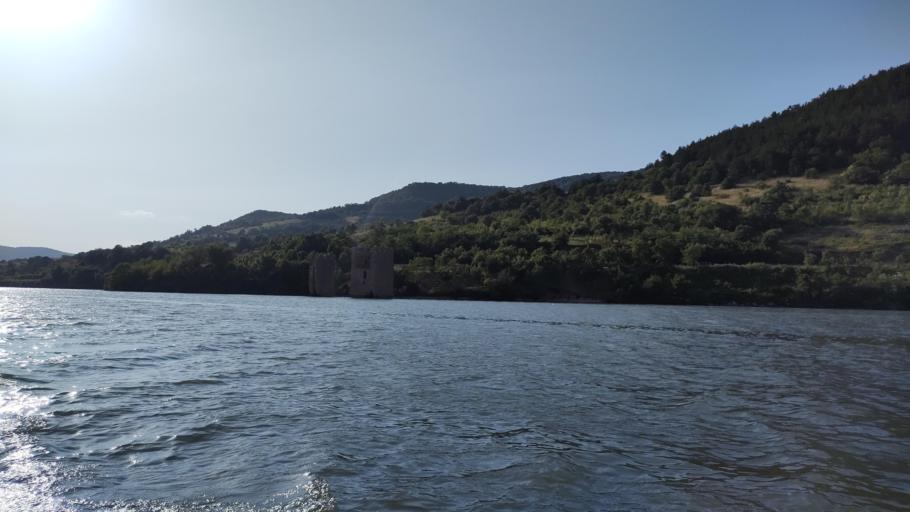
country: RO
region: Mehedinti
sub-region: Comuna Svinita
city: Svinita
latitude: 44.4789
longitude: 22.1444
